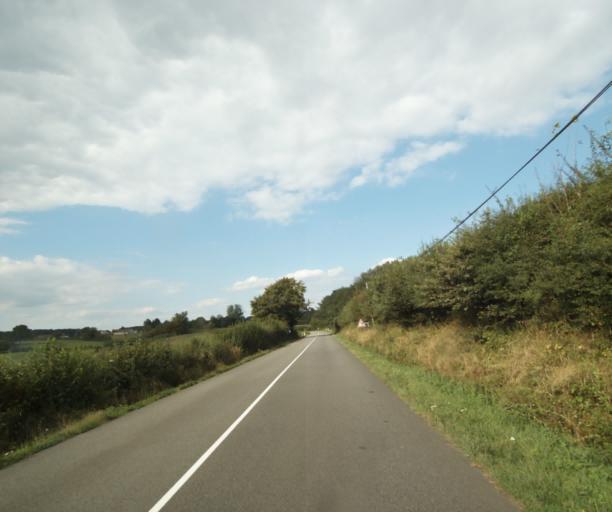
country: FR
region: Bourgogne
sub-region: Departement de Saone-et-Loire
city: Palinges
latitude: 46.5162
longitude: 4.2554
